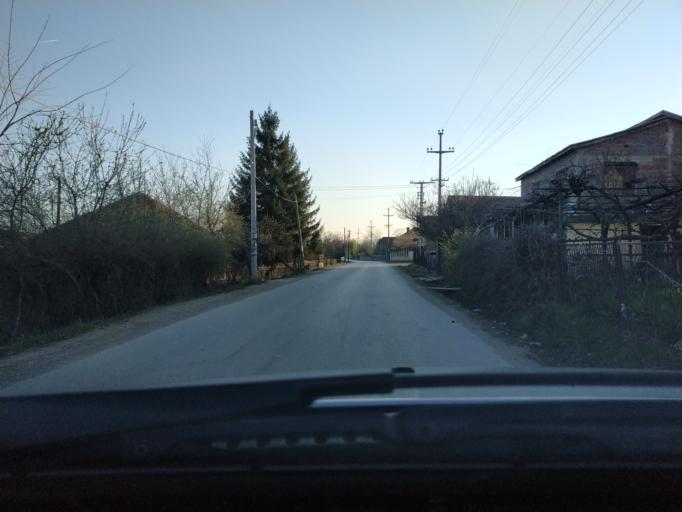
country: RS
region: Central Serbia
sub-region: Nisavski Okrug
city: Aleksinac
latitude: 43.5052
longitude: 21.7951
